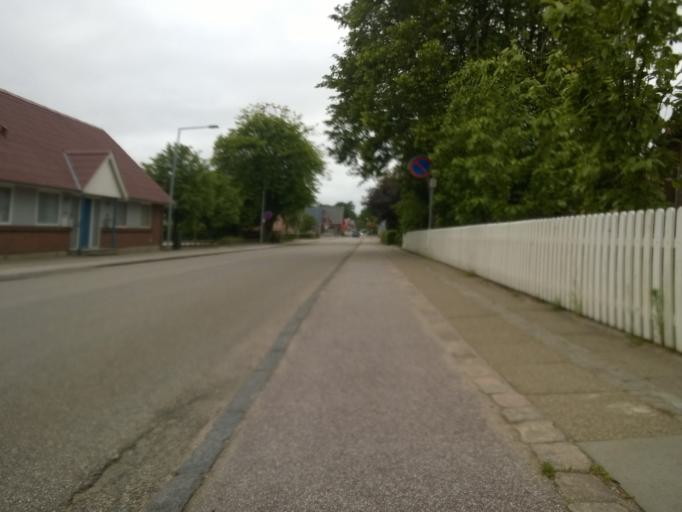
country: DK
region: Central Jutland
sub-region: Holstebro Kommune
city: Vinderup
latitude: 56.4796
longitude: 8.7807
